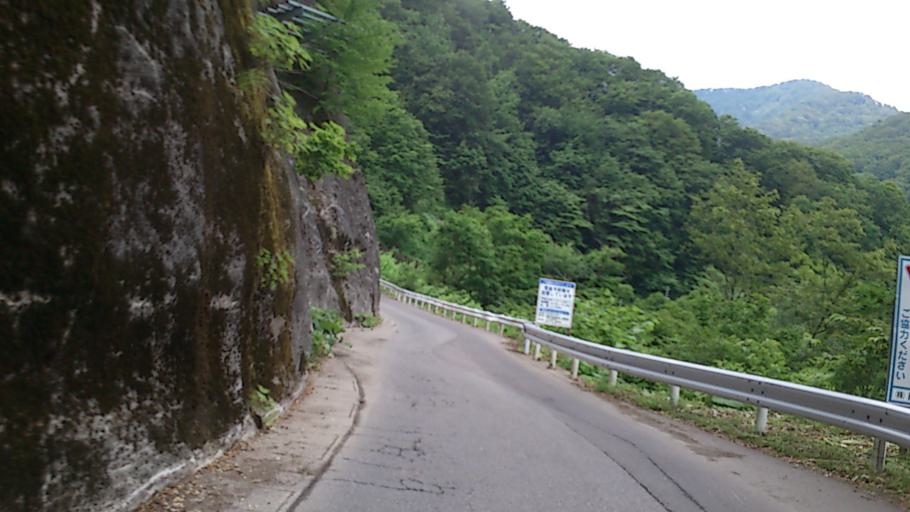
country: JP
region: Aomori
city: Hirosaki
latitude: 40.5199
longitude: 140.1778
